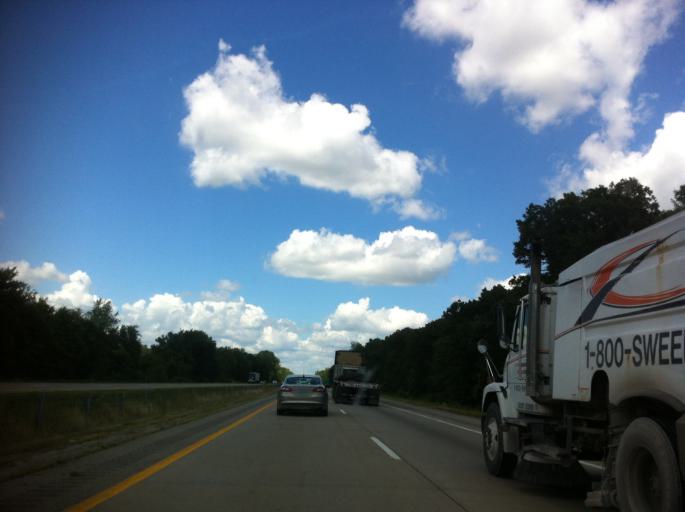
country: US
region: Michigan
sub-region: Monroe County
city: Petersburg
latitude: 41.8862
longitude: -83.6613
